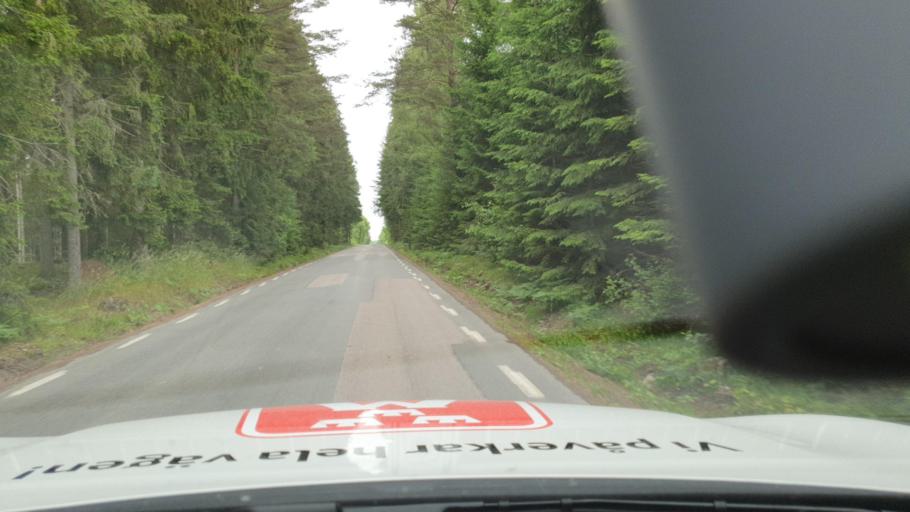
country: SE
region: Vaestra Goetaland
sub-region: Tibro Kommun
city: Tibro
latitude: 58.3757
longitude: 14.0504
